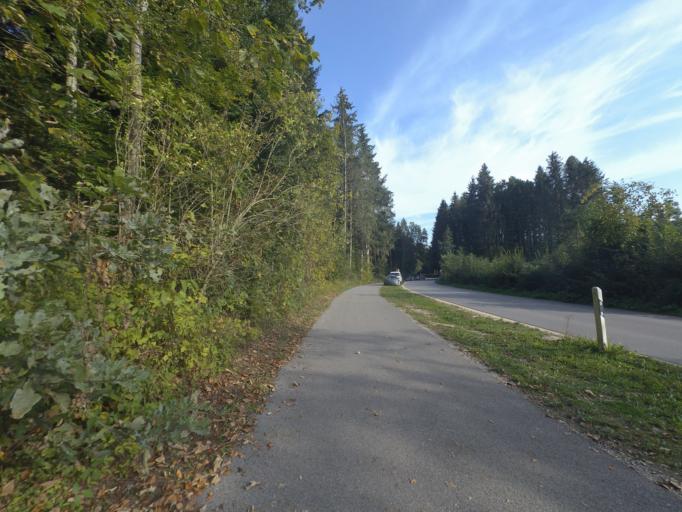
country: DE
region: Bavaria
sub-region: Upper Bavaria
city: Laufen
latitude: 47.9179
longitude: 12.9030
